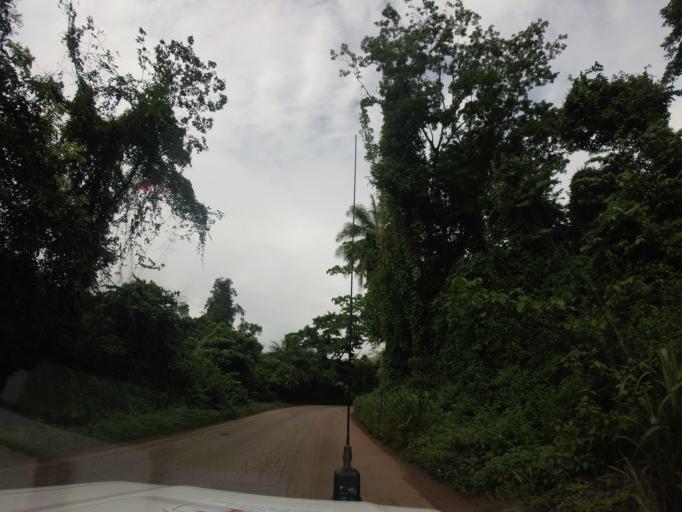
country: GN
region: Kindia
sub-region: Coyah
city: Coyah
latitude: 9.7430
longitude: -13.3655
